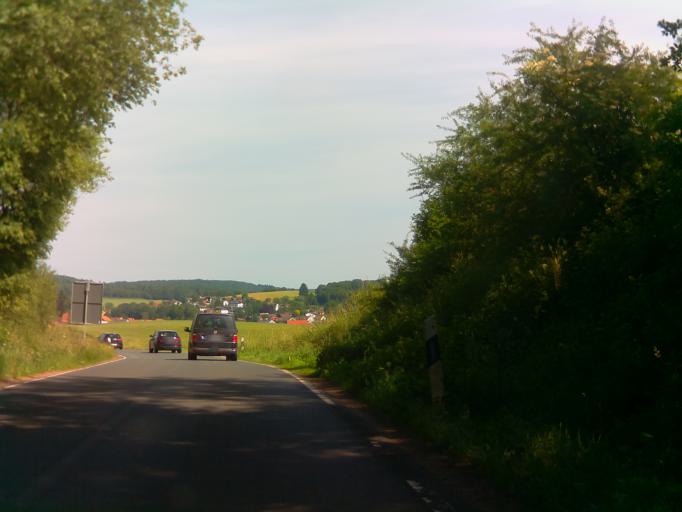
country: DE
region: Hesse
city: Rosenthal
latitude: 50.9672
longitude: 8.8717
